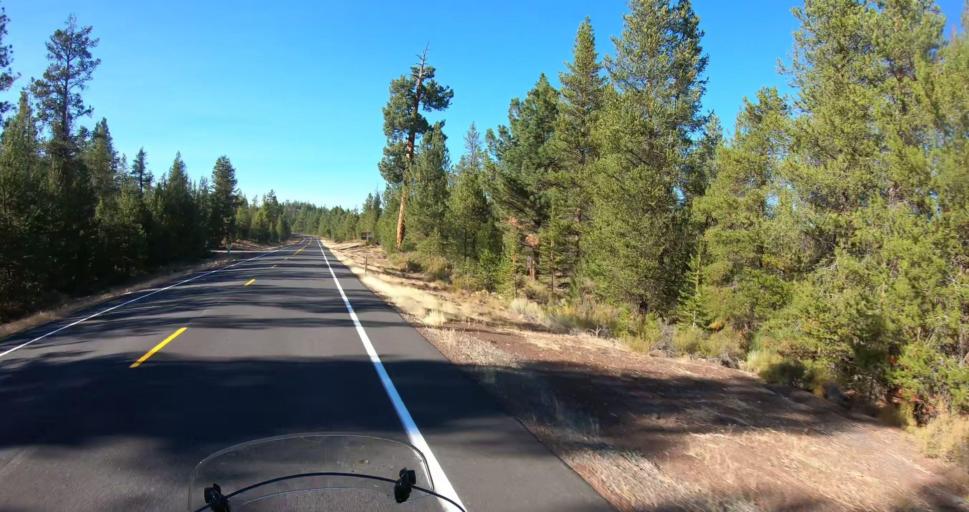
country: US
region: Oregon
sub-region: Deschutes County
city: La Pine
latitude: 43.4638
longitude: -121.3848
